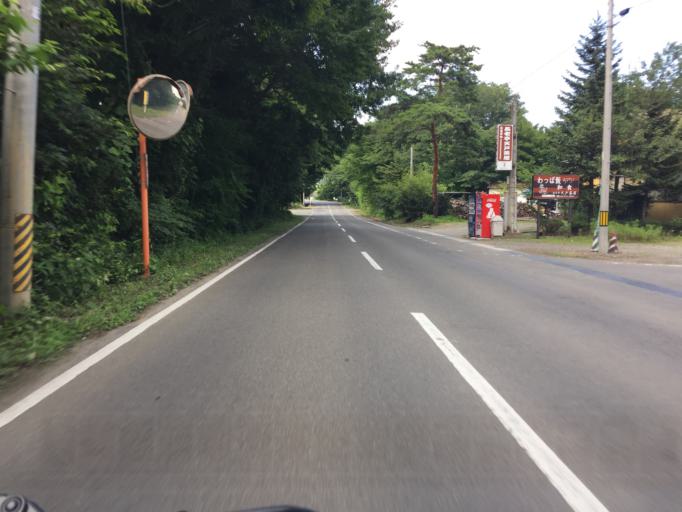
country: JP
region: Fukushima
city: Fukushima-shi
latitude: 37.7639
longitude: 140.3612
